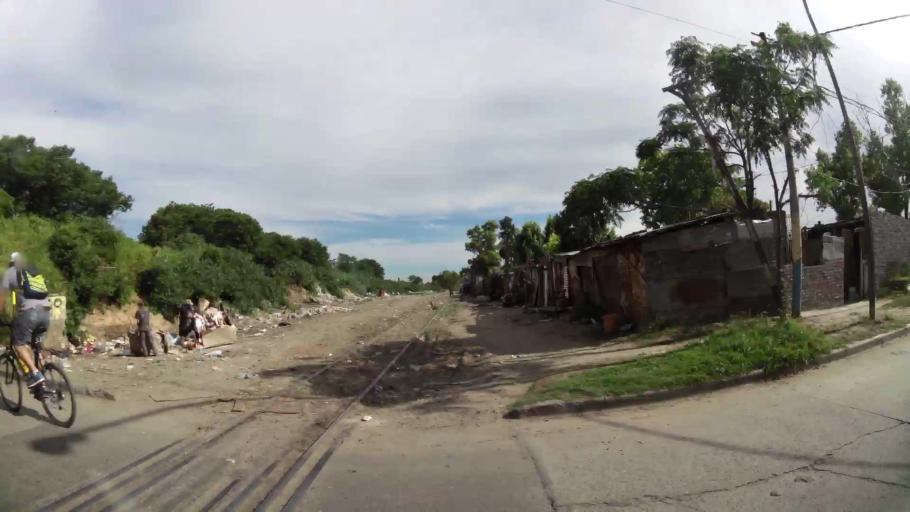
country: AR
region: Santa Fe
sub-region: Departamento de Rosario
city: Rosario
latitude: -32.9155
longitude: -60.6939
